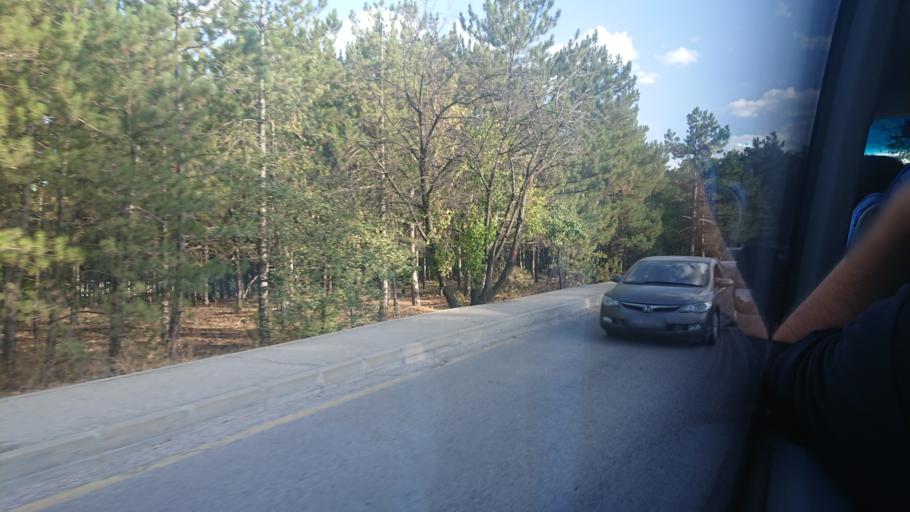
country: TR
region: Ankara
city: Ankara
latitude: 39.8905
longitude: 32.7843
